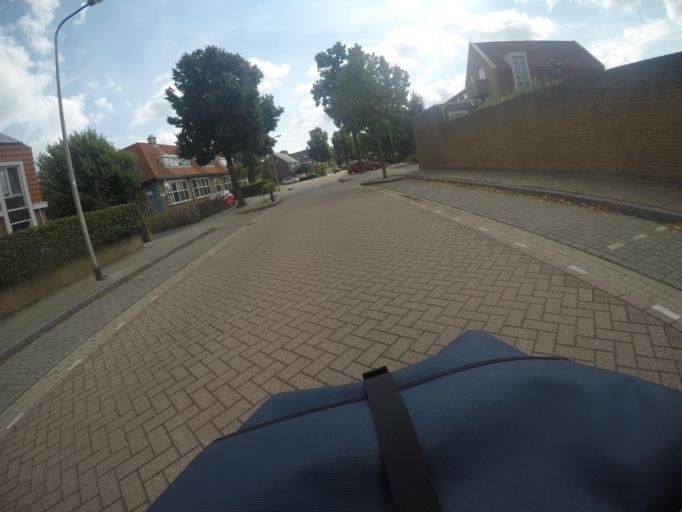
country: NL
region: Utrecht
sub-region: Gemeente Zeist
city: Zeist
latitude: 52.0956
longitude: 5.2401
